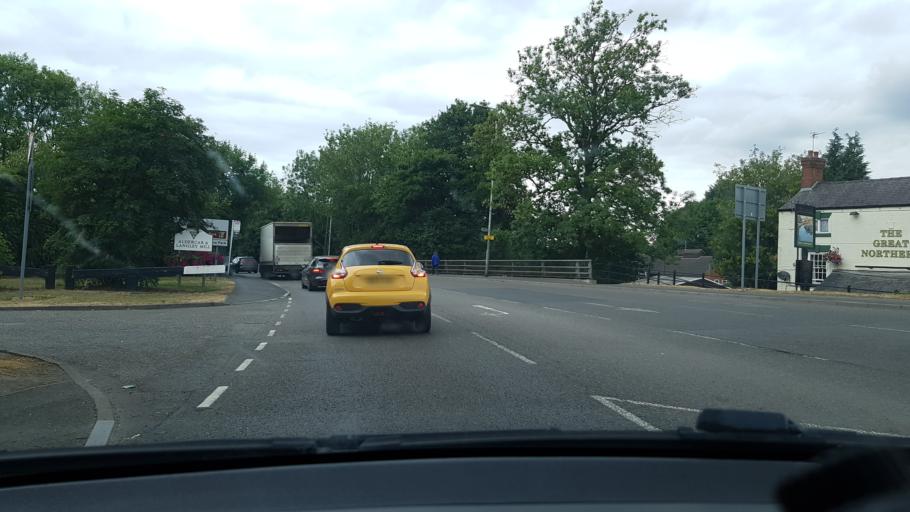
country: GB
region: England
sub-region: Nottinghamshire
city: Eastwood
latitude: 53.0191
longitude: -1.3232
